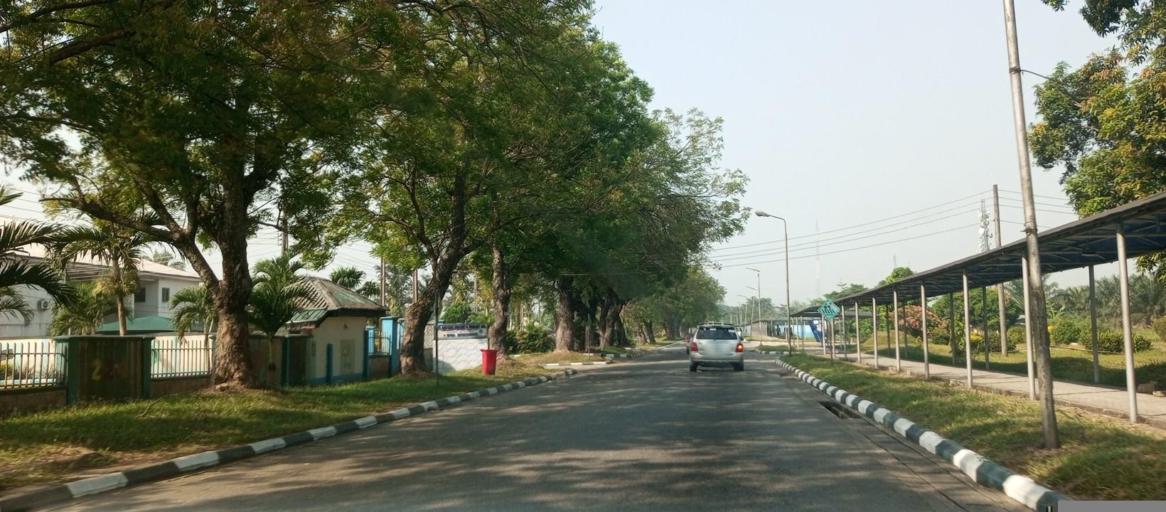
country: NG
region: Rivers
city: Emuoha
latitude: 4.9025
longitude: 6.9095
